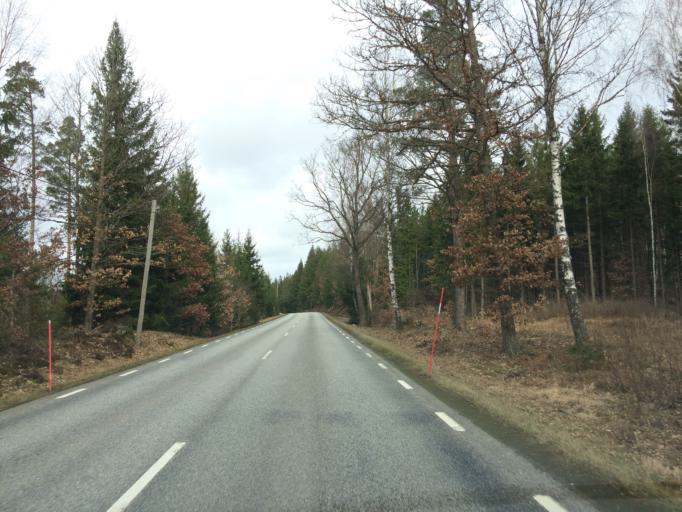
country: SE
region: Skane
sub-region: Osby Kommun
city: Lonsboda
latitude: 56.3388
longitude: 14.3148
